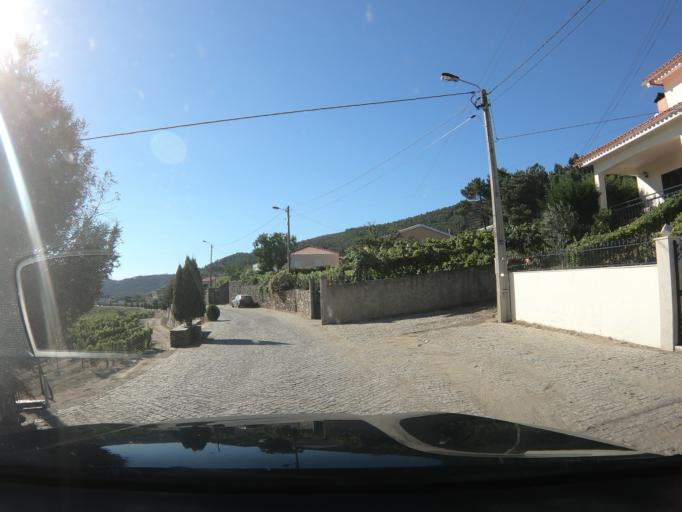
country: PT
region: Vila Real
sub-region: Sabrosa
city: Vilela
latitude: 41.2199
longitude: -7.5672
